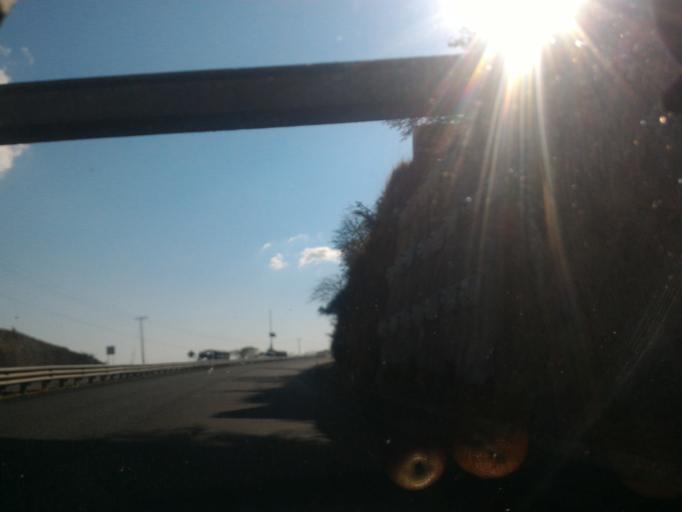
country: MX
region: Jalisco
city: Tonila
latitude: 19.4288
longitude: -103.4981
